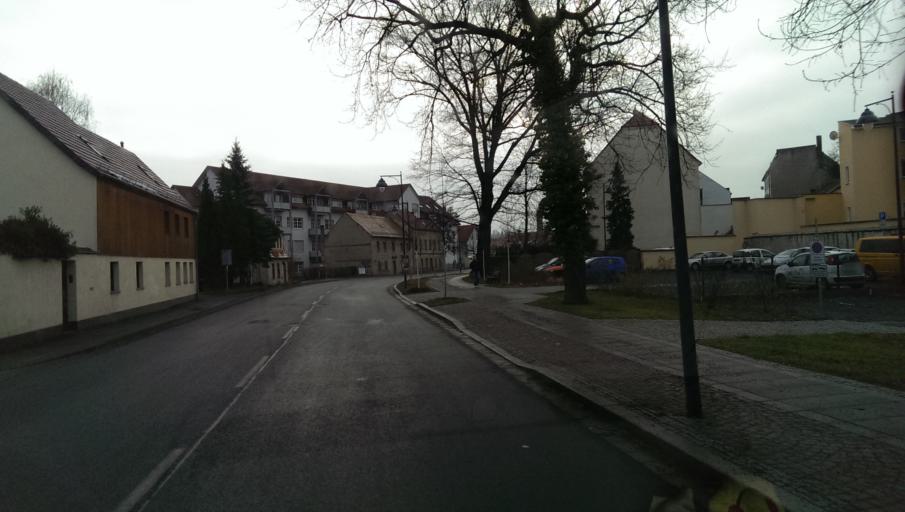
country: DE
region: Saxony
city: Grossenhain
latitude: 51.2918
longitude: 13.5347
